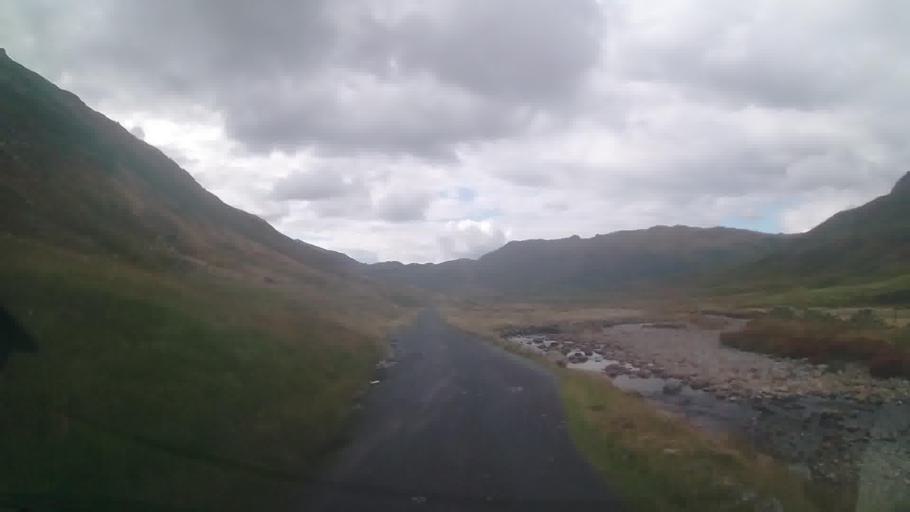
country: GB
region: England
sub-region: Cumbria
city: Ambleside
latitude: 54.4079
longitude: -3.1477
